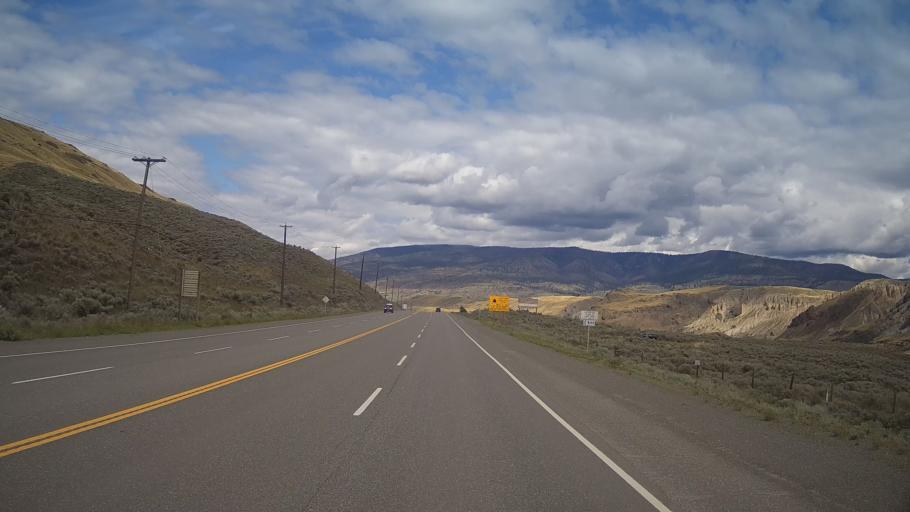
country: CA
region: British Columbia
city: Cache Creek
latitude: 50.7754
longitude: -121.3129
